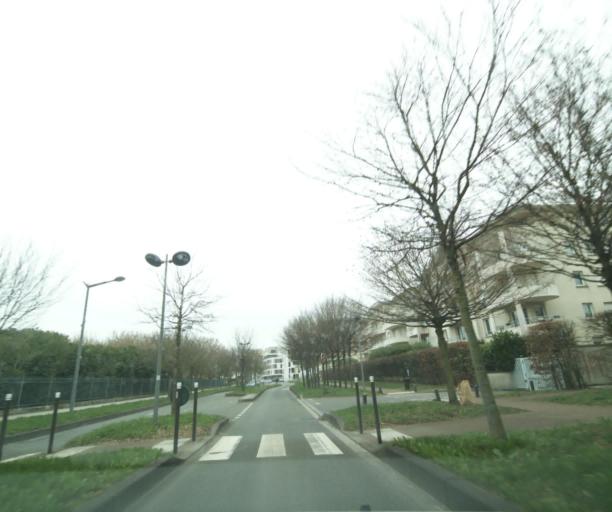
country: FR
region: Ile-de-France
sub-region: Departement du Val-d'Oise
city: Courdimanche
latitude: 49.0464
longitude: 2.0073
